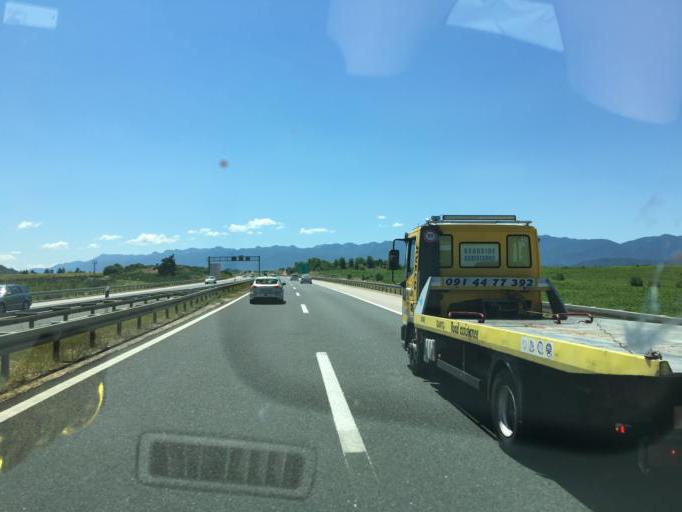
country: HR
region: Licko-Senjska
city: Gospic
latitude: 44.5656
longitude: 15.4267
